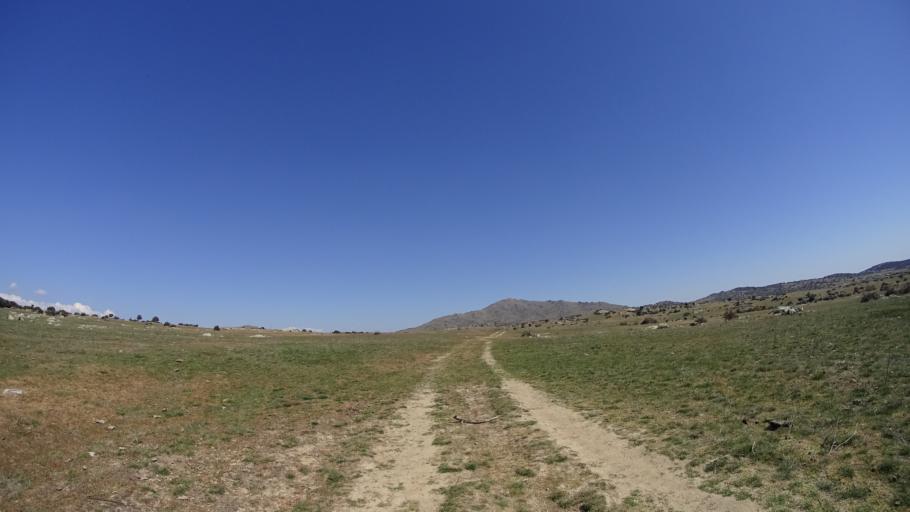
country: ES
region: Madrid
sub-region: Provincia de Madrid
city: Colmenar Viejo
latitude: 40.7026
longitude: -3.7594
